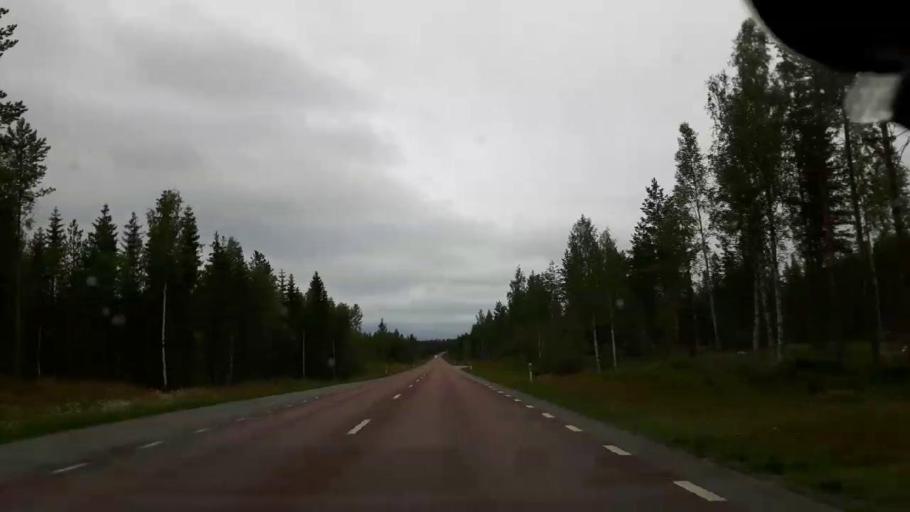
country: SE
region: Jaemtland
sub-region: Bergs Kommun
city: Hoverberg
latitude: 62.8128
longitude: 14.5176
